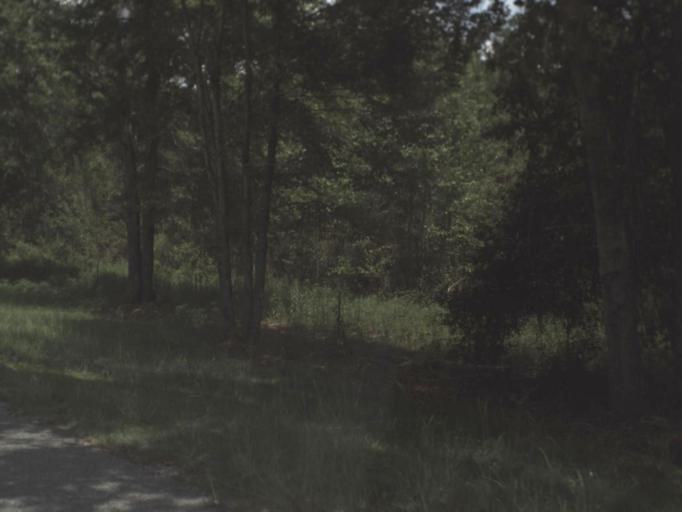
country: US
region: Florida
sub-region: Madison County
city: Madison
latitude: 30.4866
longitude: -83.2095
